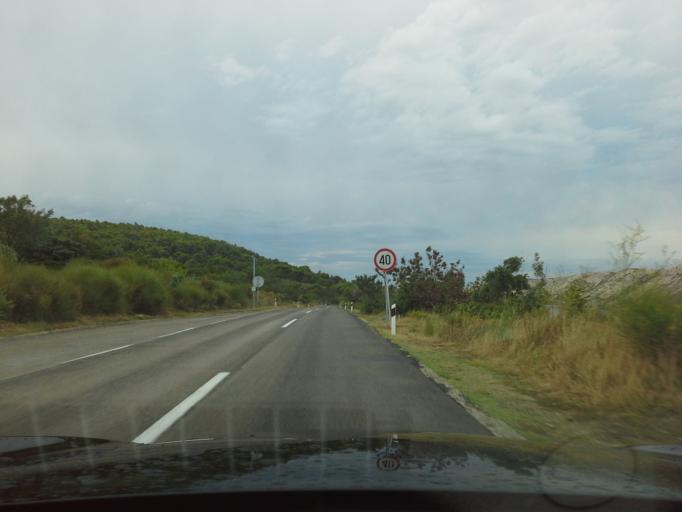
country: HR
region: Primorsko-Goranska
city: Banjol
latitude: 44.7212
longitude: 14.8226
